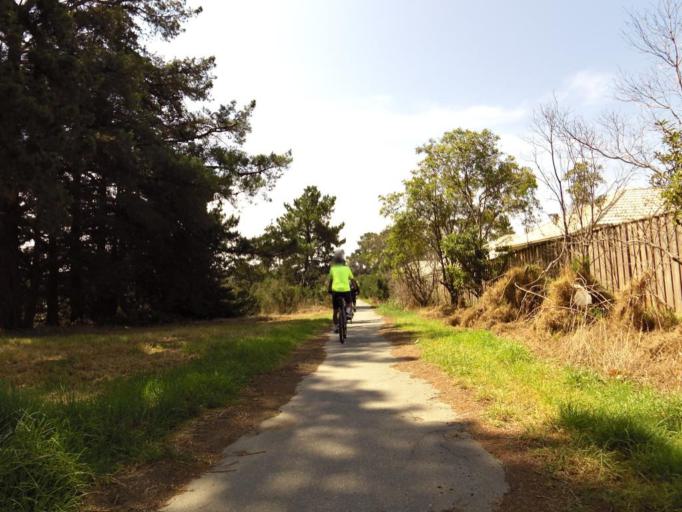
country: AU
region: Victoria
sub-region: Mornington Peninsula
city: Hastings
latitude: -38.2868
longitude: 145.1881
